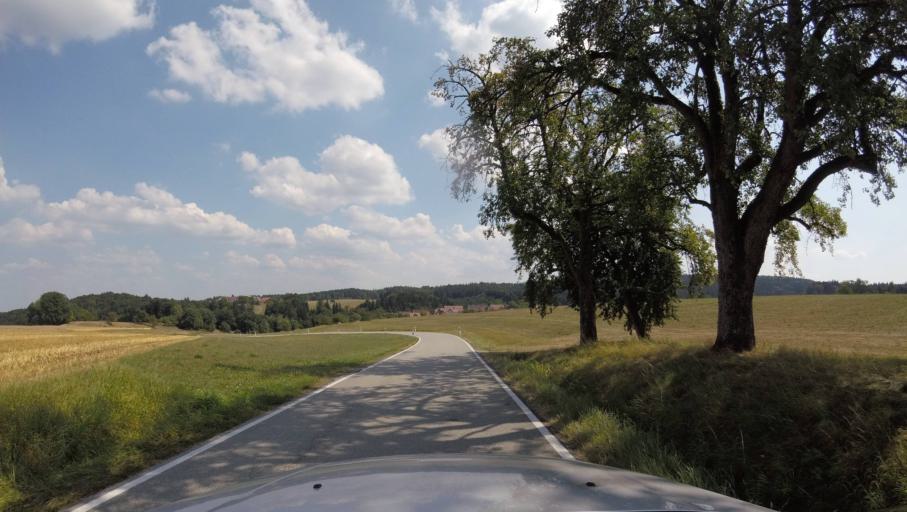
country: DE
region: Baden-Wuerttemberg
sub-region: Regierungsbezirk Stuttgart
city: Althutte
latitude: 48.9474
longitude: 9.5917
